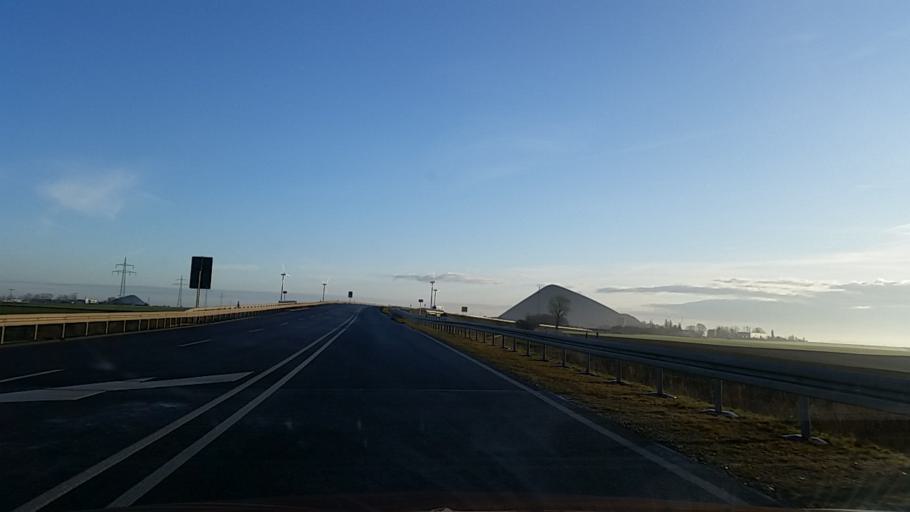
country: DE
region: Saxony-Anhalt
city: Siersleben
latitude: 51.5848
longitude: 11.5318
